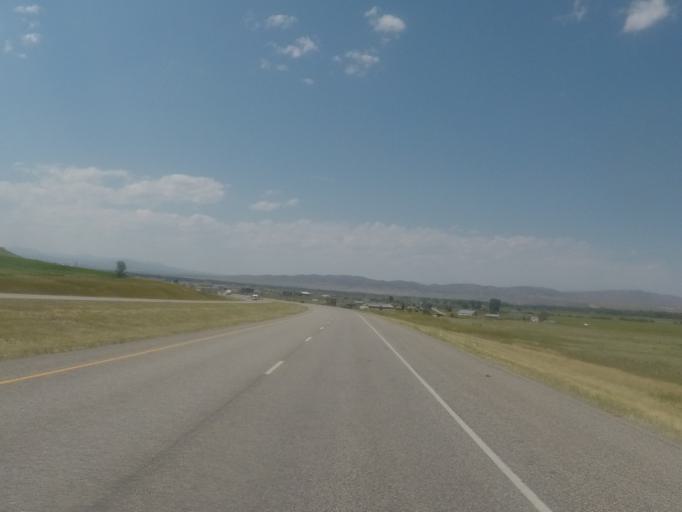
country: US
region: Montana
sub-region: Gallatin County
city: Three Forks
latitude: 45.8866
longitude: -111.4552
